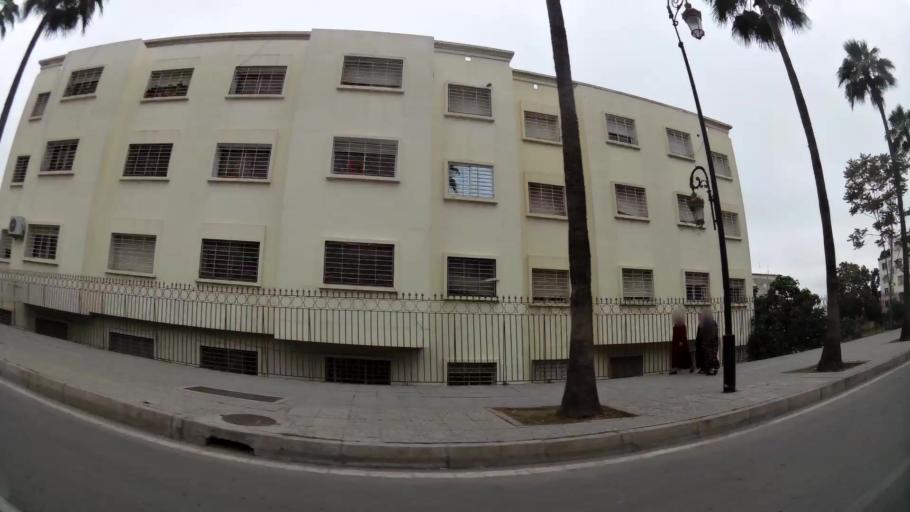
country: MA
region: Fes-Boulemane
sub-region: Fes
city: Fes
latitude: 34.0486
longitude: -4.9960
